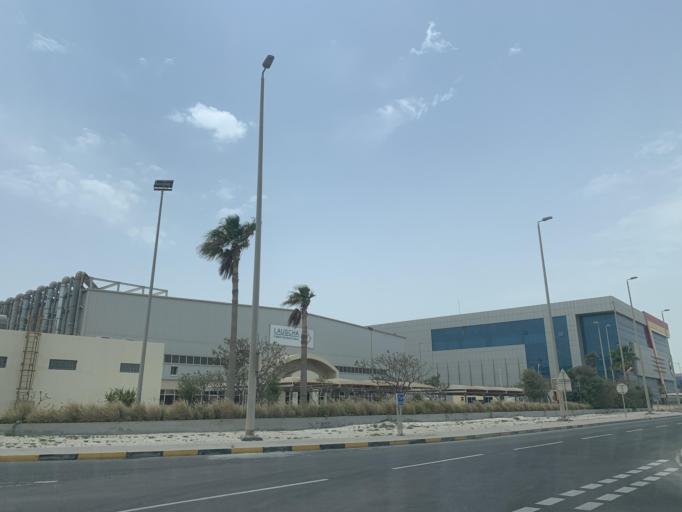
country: BH
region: Muharraq
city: Al Hadd
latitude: 26.2182
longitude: 50.6819
